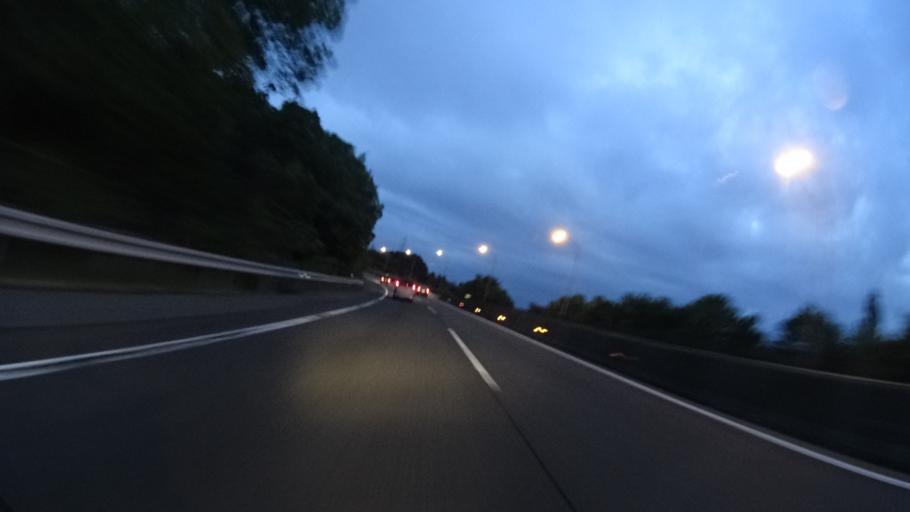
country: JP
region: Shiga Prefecture
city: Hikone
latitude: 35.1702
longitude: 136.2746
